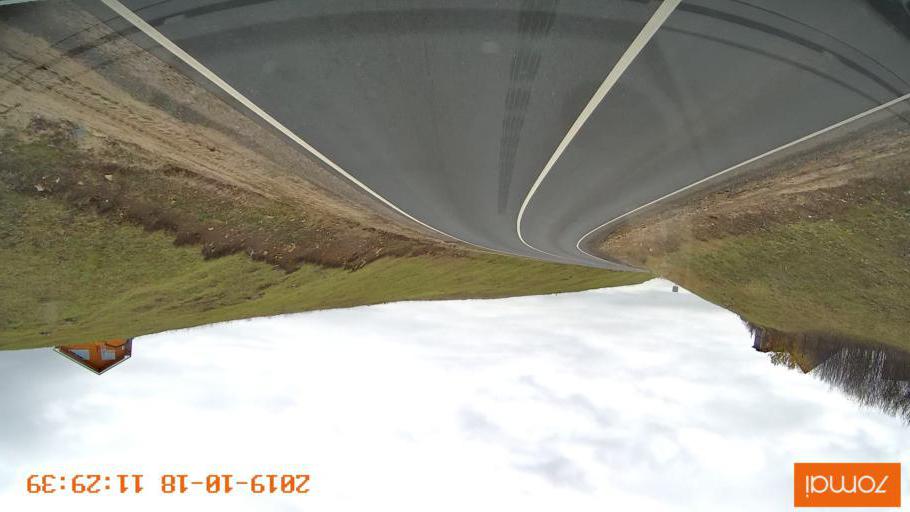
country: RU
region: Rjazan
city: Oktyabr'skiy
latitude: 54.1557
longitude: 38.6792
